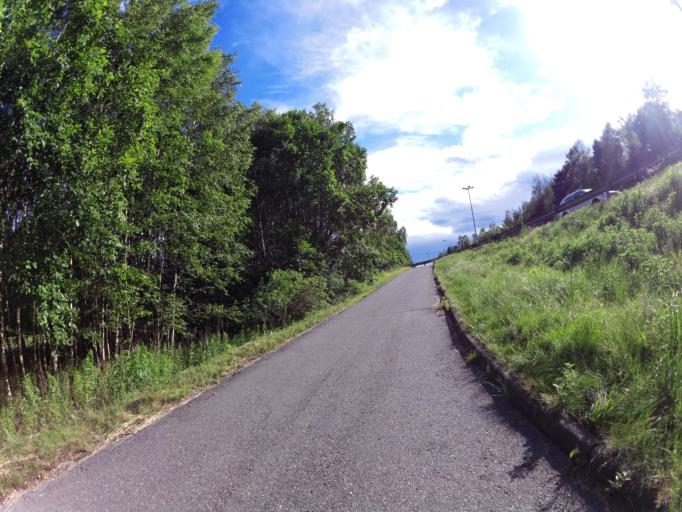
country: NO
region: Ostfold
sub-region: Fredrikstad
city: Fredrikstad
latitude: 59.2608
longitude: 11.0054
